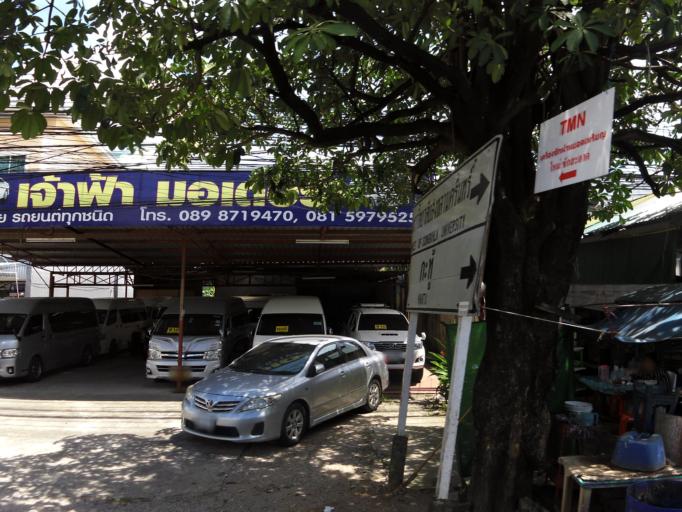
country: TH
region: Phuket
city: Mueang Phuket
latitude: 7.8697
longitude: 98.3585
